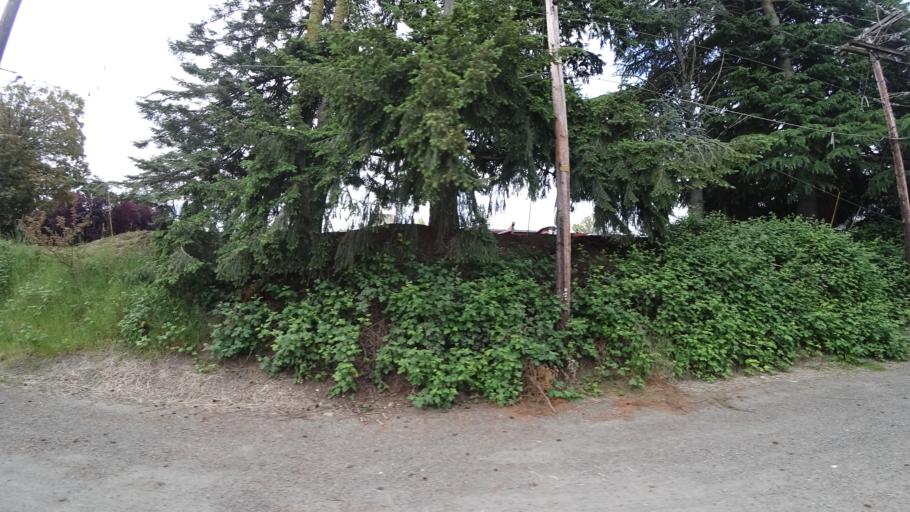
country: US
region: Oregon
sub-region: Washington County
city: Garden Home-Whitford
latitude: 45.4666
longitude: -122.7485
